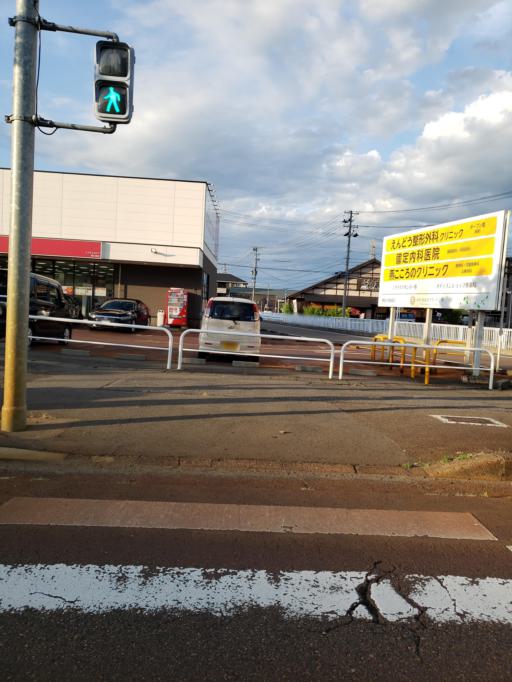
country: JP
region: Niigata
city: Tsubame
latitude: 37.6493
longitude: 138.9359
